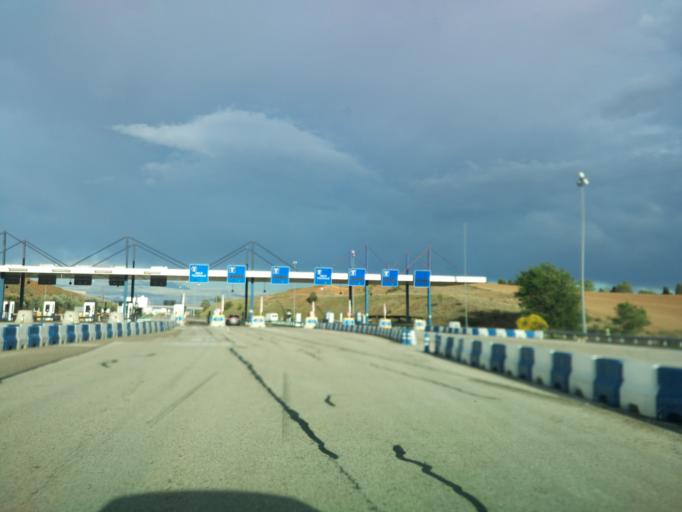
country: ES
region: Madrid
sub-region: Provincia de Madrid
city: Ajalvir
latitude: 40.5078
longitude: -3.4865
